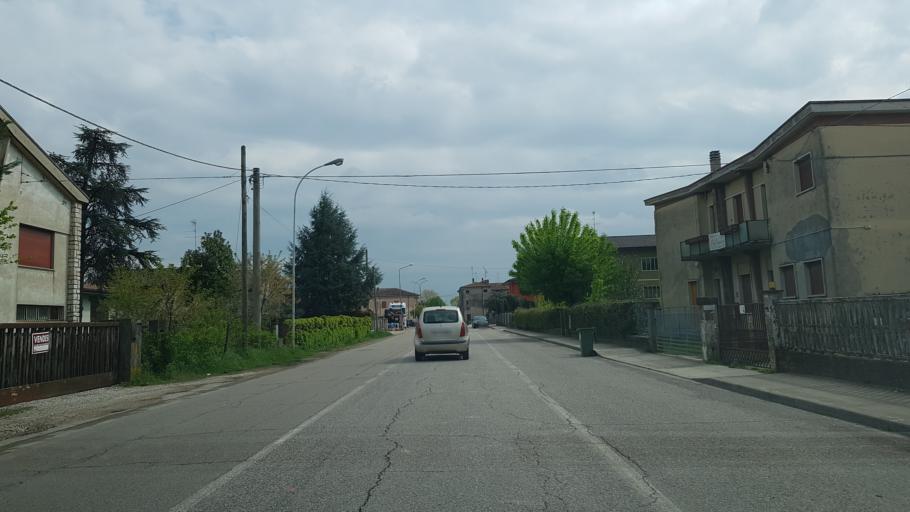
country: IT
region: Veneto
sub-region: Provincia di Verona
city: Maccacari
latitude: 45.1445
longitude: 11.1349
